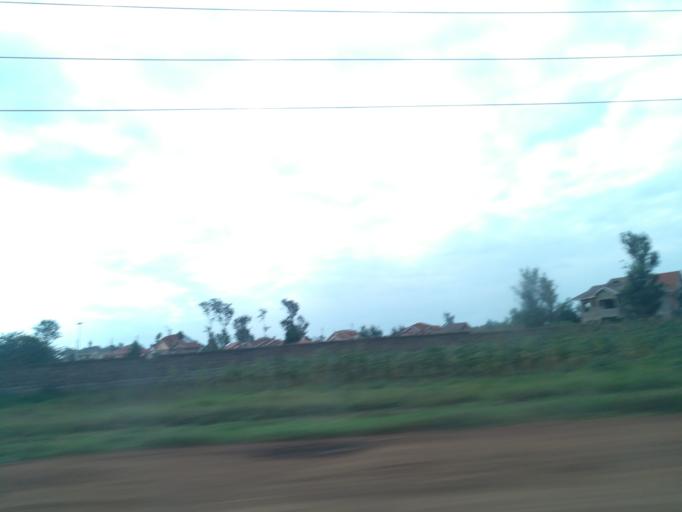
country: KE
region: Nairobi Area
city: Thika
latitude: -1.0379
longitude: 37.0608
